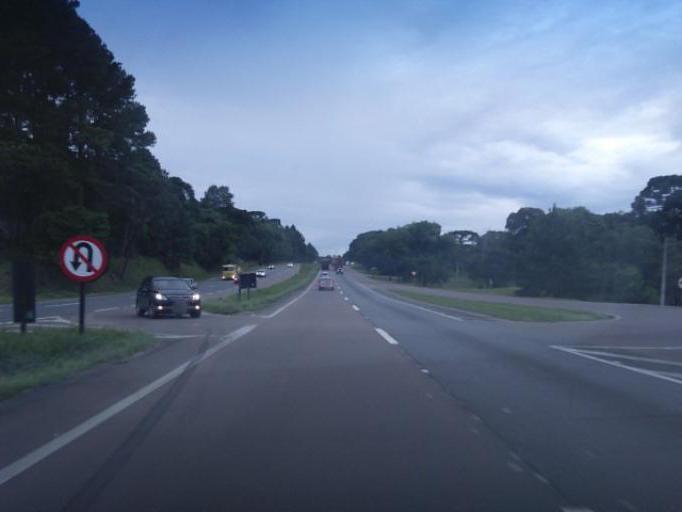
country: BR
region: Parana
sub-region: Sao Jose Dos Pinhais
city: Sao Jose dos Pinhais
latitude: -25.6892
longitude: -49.1461
